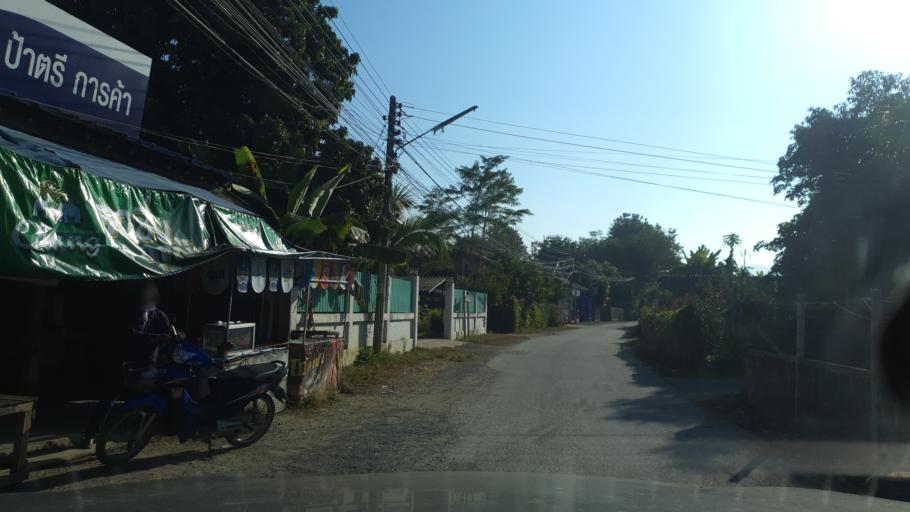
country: TH
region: Chiang Mai
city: San Kamphaeng
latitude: 18.7154
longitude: 99.1459
